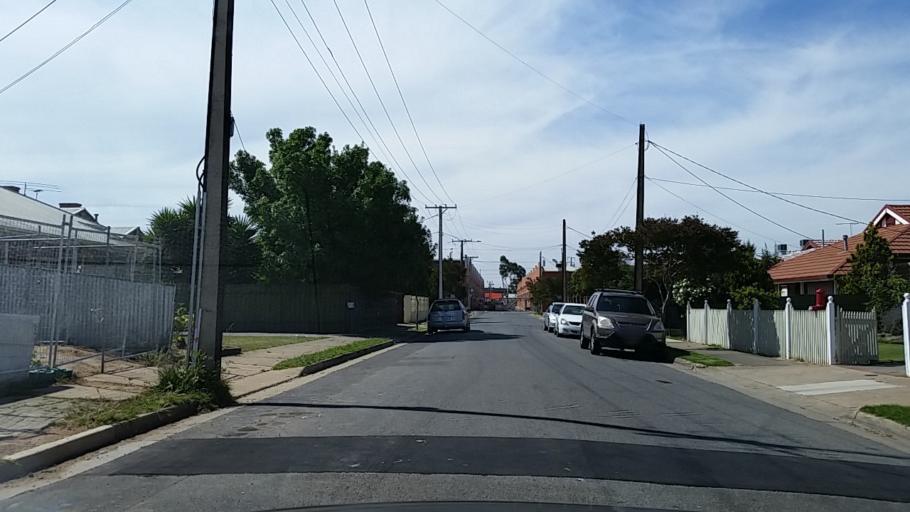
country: AU
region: South Australia
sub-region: Charles Sturt
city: Albert Park
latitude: -34.8734
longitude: 138.5199
